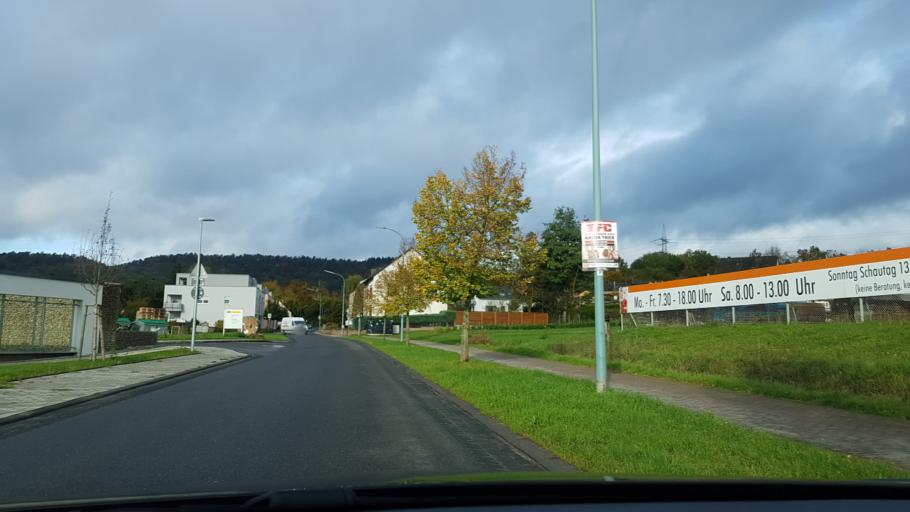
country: DE
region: Rheinland-Pfalz
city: Schweich
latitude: 49.8288
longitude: 6.7412
